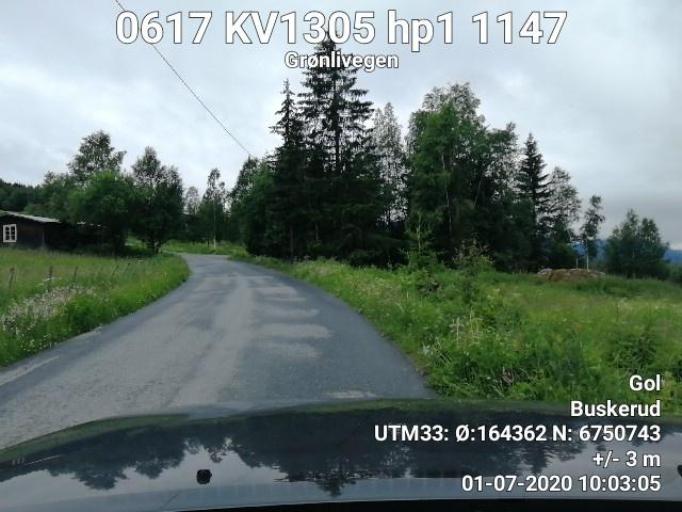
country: NO
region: Buskerud
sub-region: Gol
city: Gol
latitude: 60.7502
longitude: 8.8364
